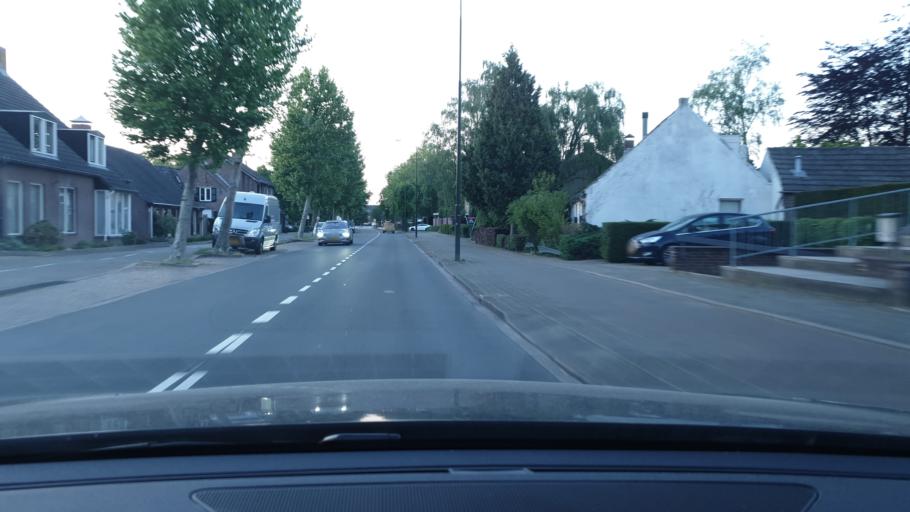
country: NL
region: North Brabant
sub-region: Gemeente Waalre
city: Waalre
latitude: 51.3900
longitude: 5.4444
